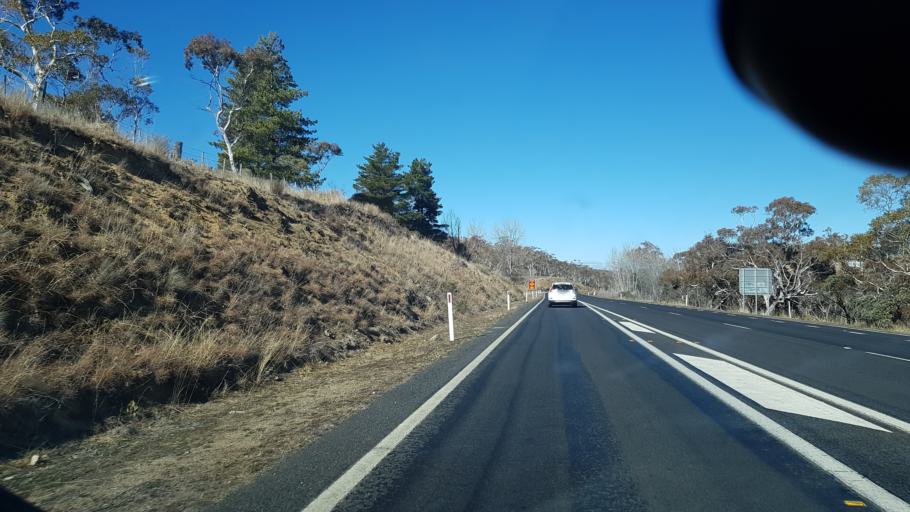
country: AU
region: New South Wales
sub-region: Snowy River
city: Jindabyne
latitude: -36.4152
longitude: 148.6417
